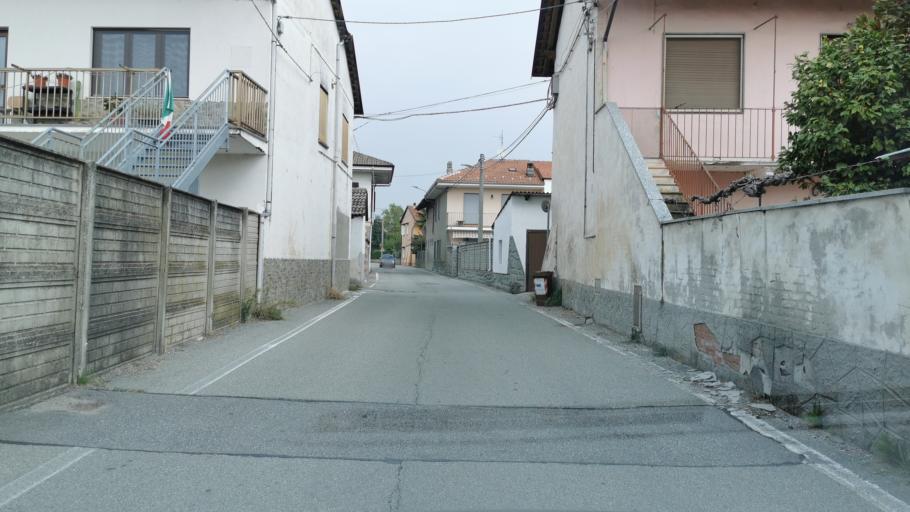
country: IT
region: Piedmont
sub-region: Provincia di Torino
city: Tonengo-Casale
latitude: 45.2915
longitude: 7.9437
